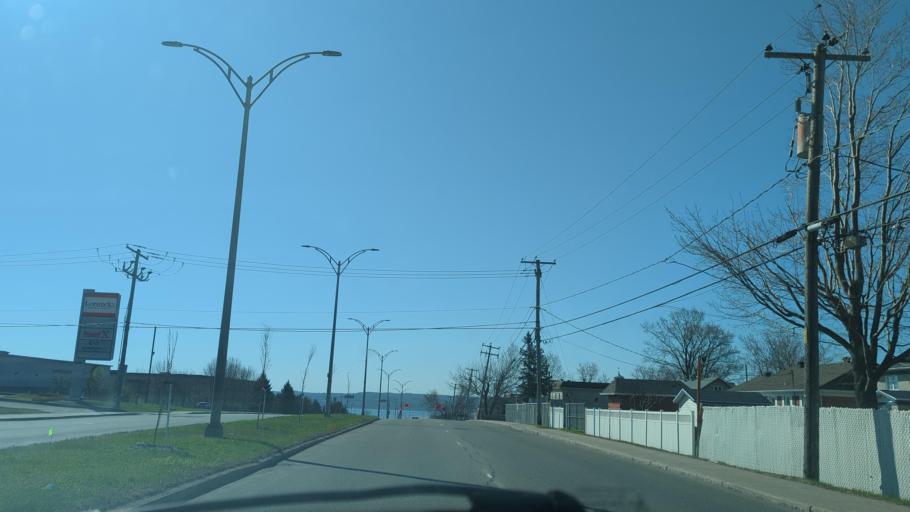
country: CA
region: Quebec
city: Quebec
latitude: 46.8597
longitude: -71.2220
